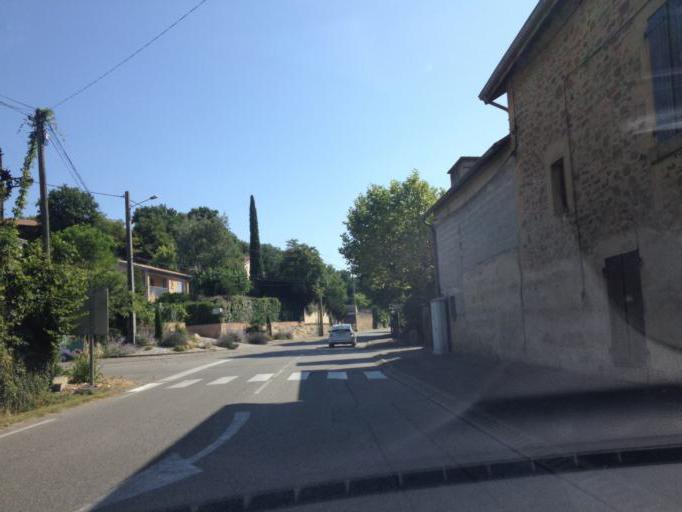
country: FR
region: Rhone-Alpes
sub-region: Departement de la Drome
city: Clerieux
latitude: 45.1196
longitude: 4.9716
